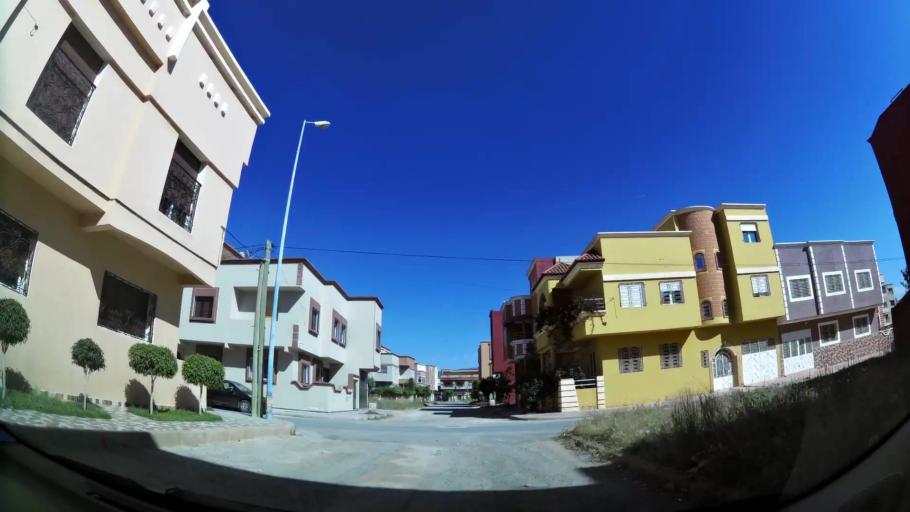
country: MA
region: Oriental
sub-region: Berkane-Taourirt
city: Berkane
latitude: 34.9431
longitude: -2.3393
